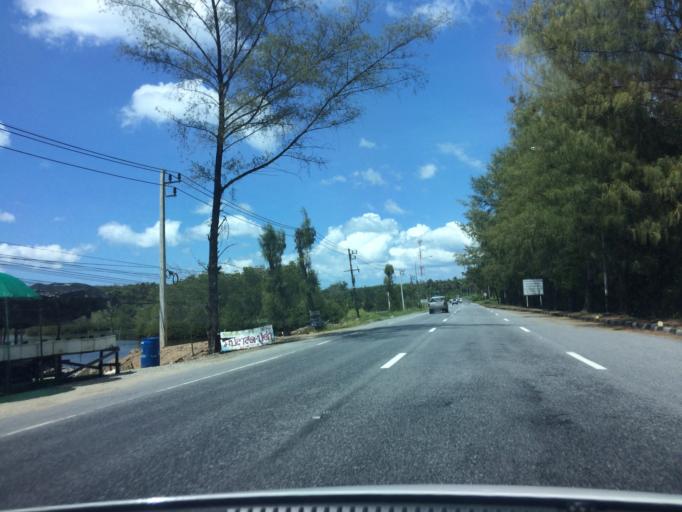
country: TH
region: Phuket
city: Thalang
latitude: 8.2098
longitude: 98.2986
